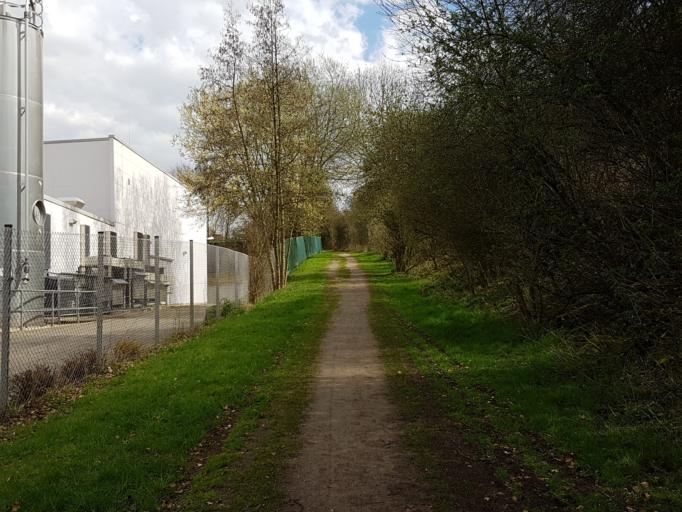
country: DE
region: North Rhine-Westphalia
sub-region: Regierungsbezirk Koln
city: Wurselen
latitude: 50.7879
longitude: 6.1402
